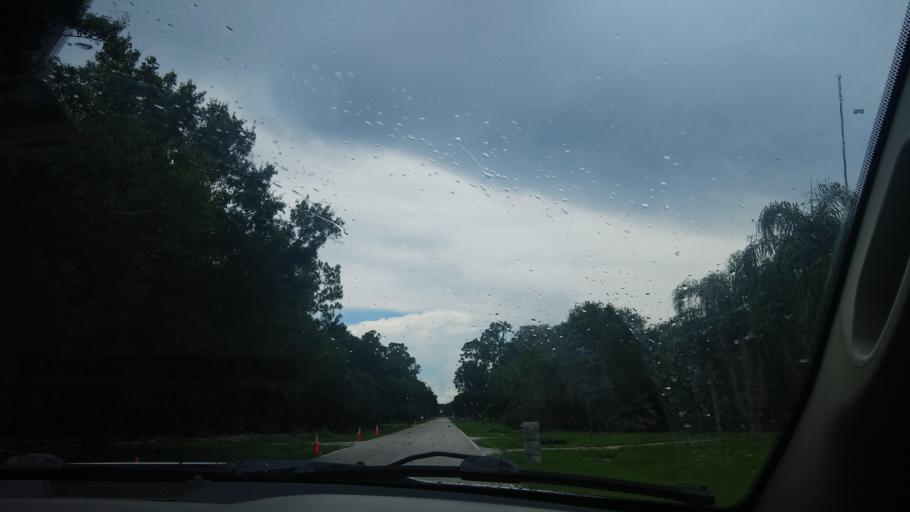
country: US
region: Florida
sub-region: Indian River County
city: Fellsmere
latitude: 27.7649
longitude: -80.6014
